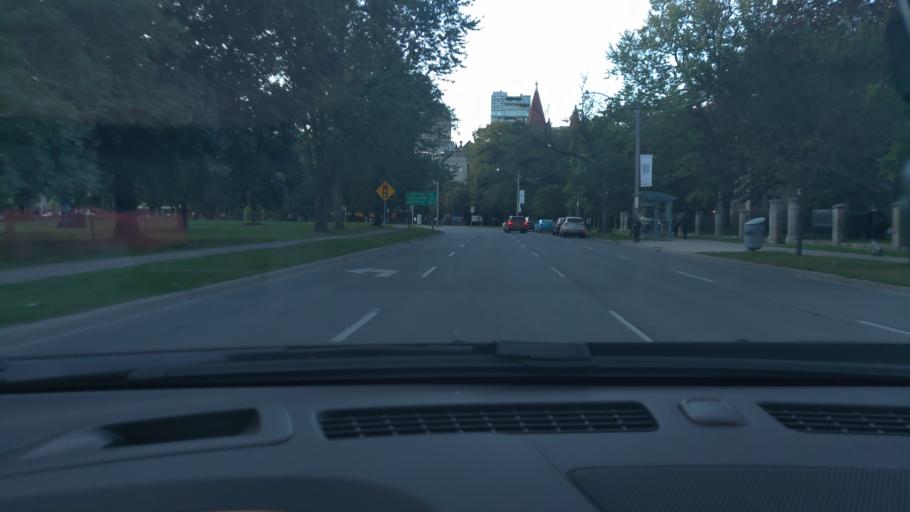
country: CA
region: Ontario
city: Toronto
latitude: 43.6649
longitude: -79.3912
